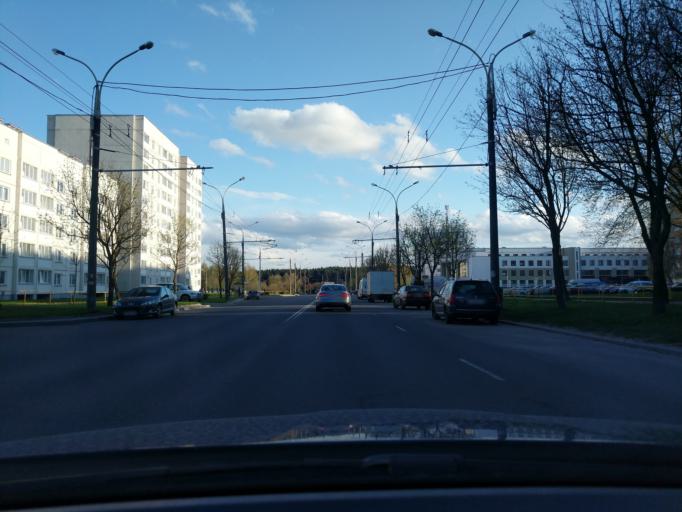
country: BY
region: Minsk
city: Novoye Medvezhino
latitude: 53.8958
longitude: 27.4526
